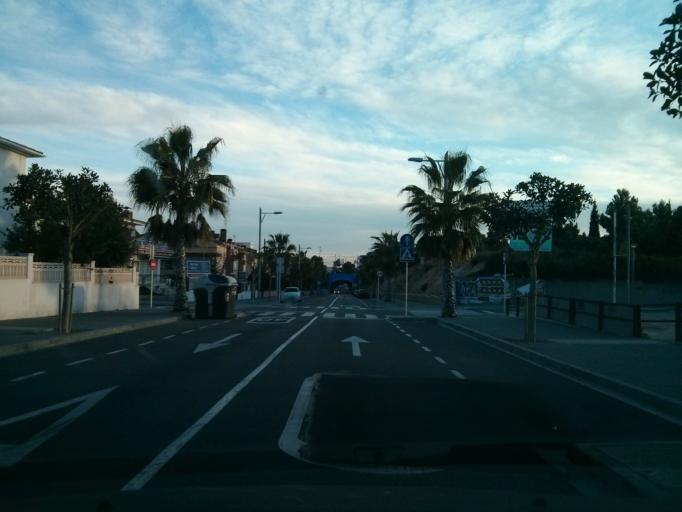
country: ES
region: Catalonia
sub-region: Provincia de Tarragona
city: El Vendrell
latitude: 41.1876
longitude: 1.5203
